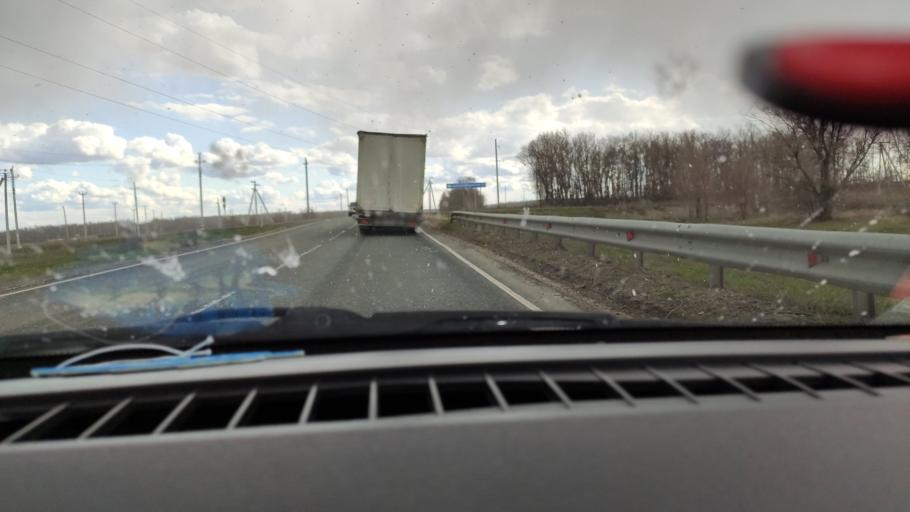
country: RU
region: Saratov
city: Balakovo
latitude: 52.1151
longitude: 47.7507
